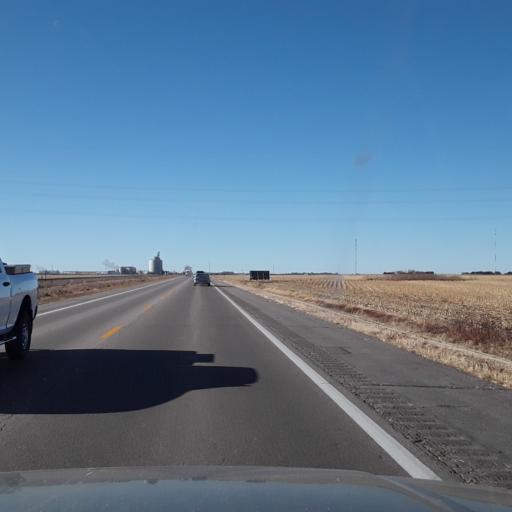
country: US
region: Nebraska
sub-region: Kearney County
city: Minden
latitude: 40.4884
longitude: -99.0539
